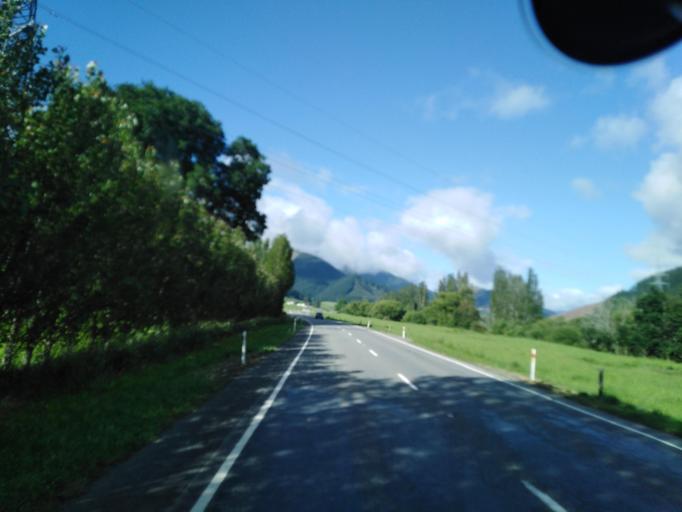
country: NZ
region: Nelson
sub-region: Nelson City
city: Nelson
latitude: -41.2885
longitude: 173.6342
